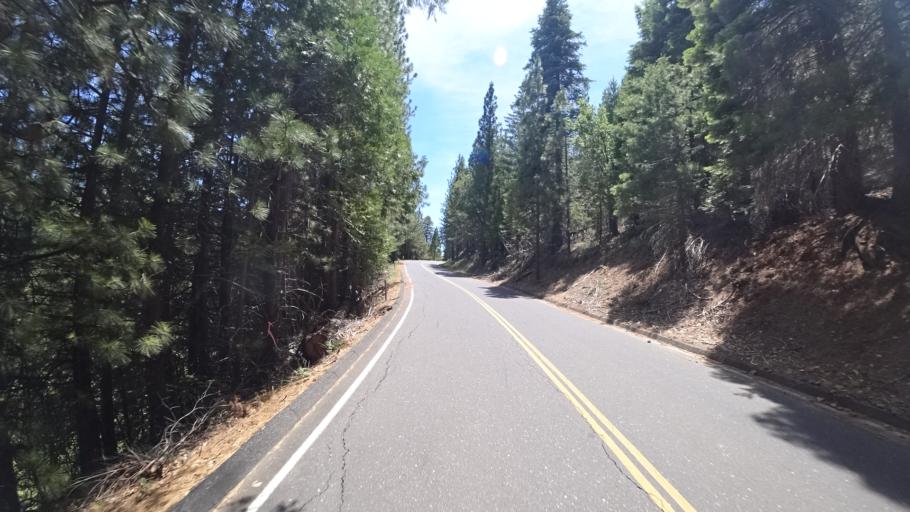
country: US
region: California
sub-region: Calaveras County
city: Arnold
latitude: 38.3099
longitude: -120.2406
